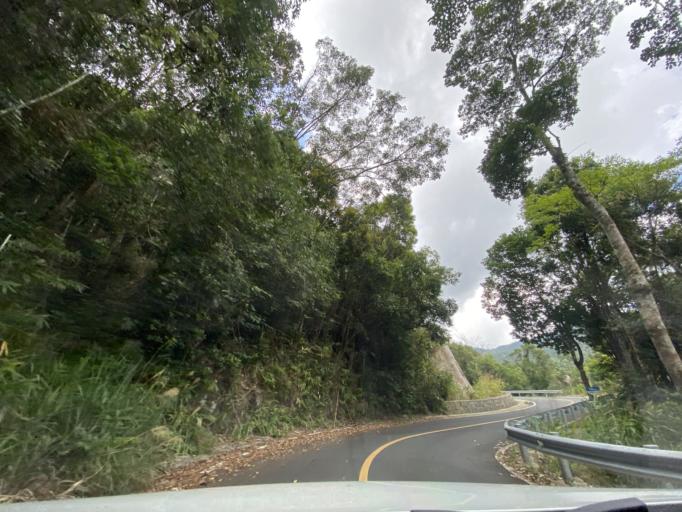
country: CN
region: Hainan
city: Benhao
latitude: 18.6812
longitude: 109.8783
